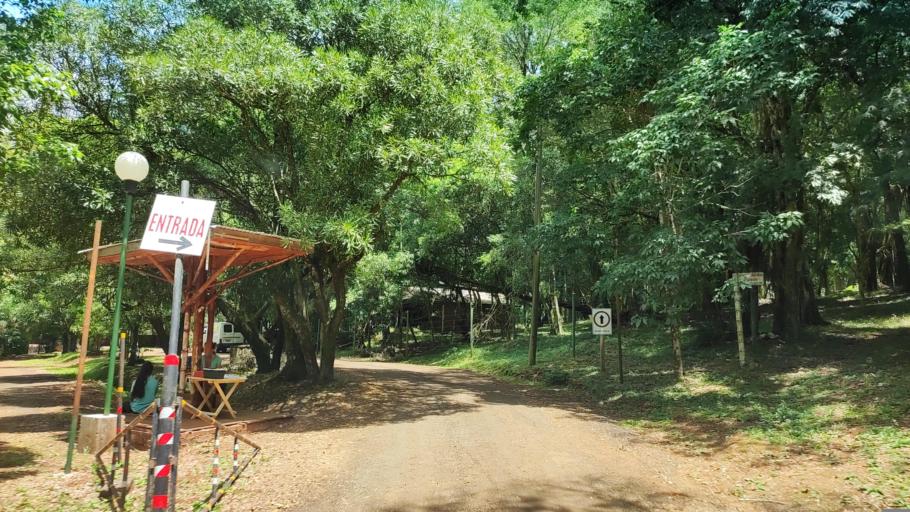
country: AR
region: Misiones
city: Ruiz de Montoya
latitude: -27.0381
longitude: -55.0366
